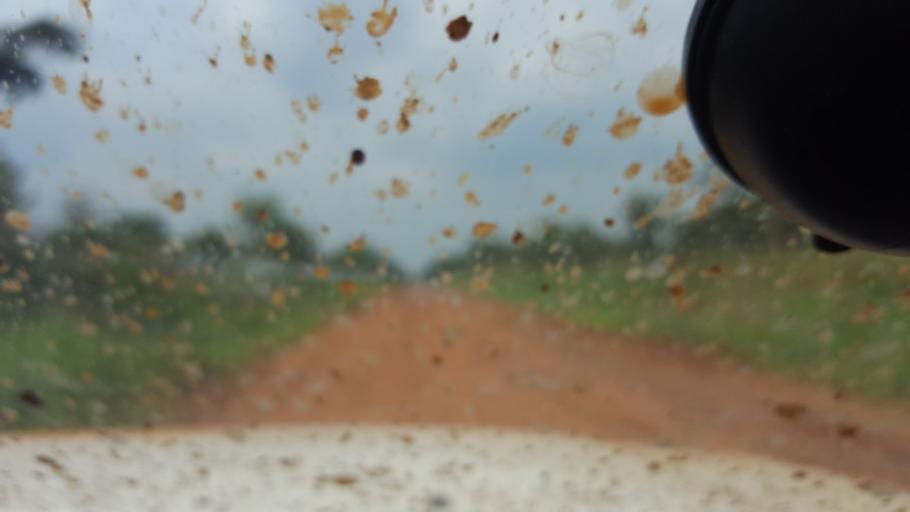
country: CD
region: Bandundu
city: Bandundu
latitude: -3.7604
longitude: 17.1523
